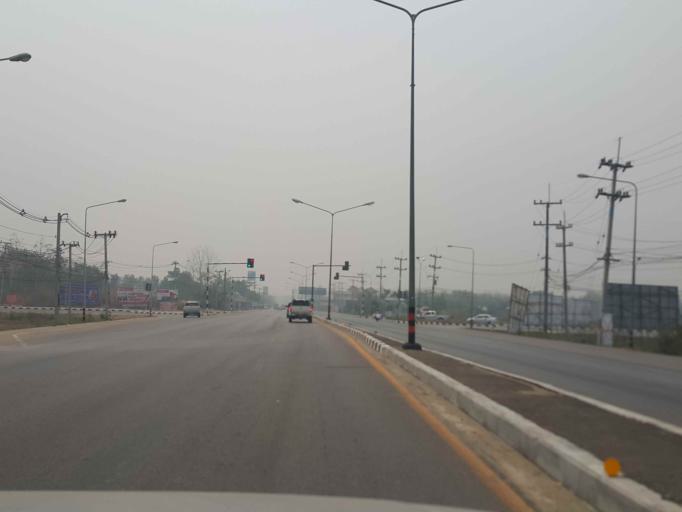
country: TH
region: Chiang Mai
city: Mae Taeng
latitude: 19.0733
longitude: 98.9385
